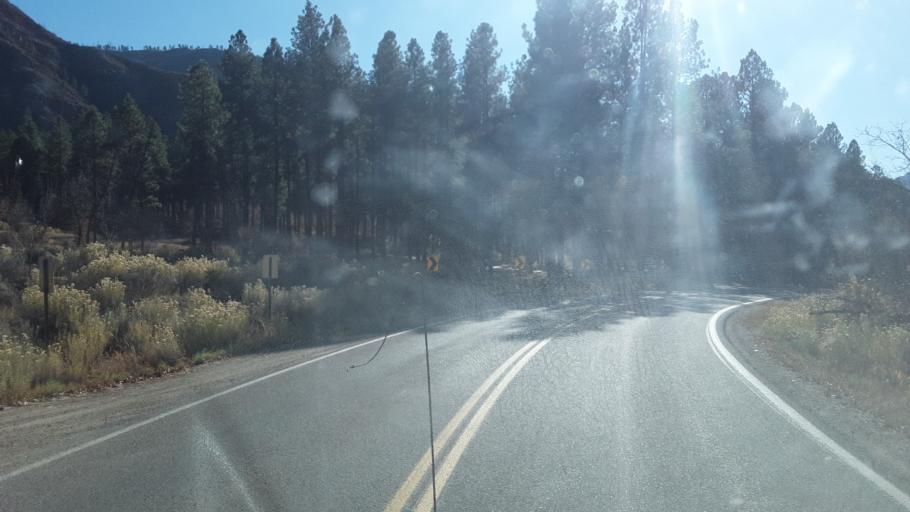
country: US
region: Colorado
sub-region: La Plata County
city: Durango
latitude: 37.4013
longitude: -107.8171
